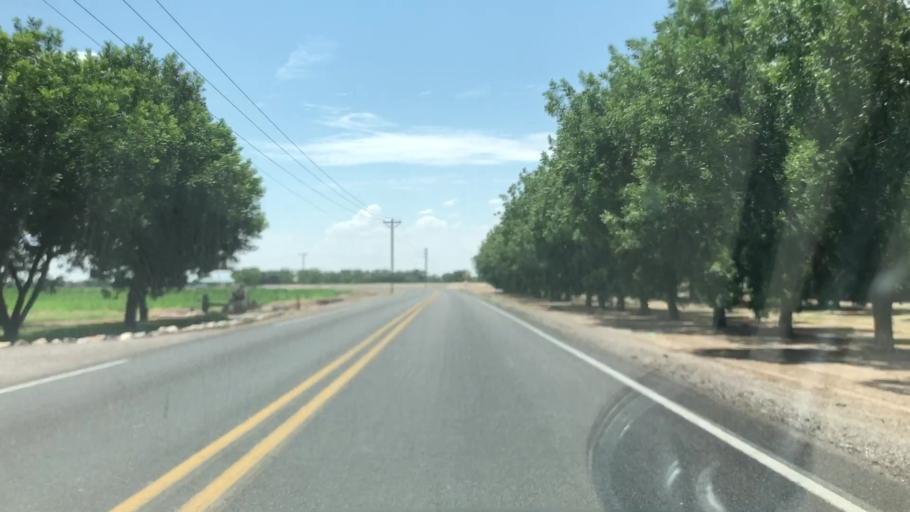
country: US
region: New Mexico
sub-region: Dona Ana County
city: Vado
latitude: 32.0954
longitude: -106.6836
